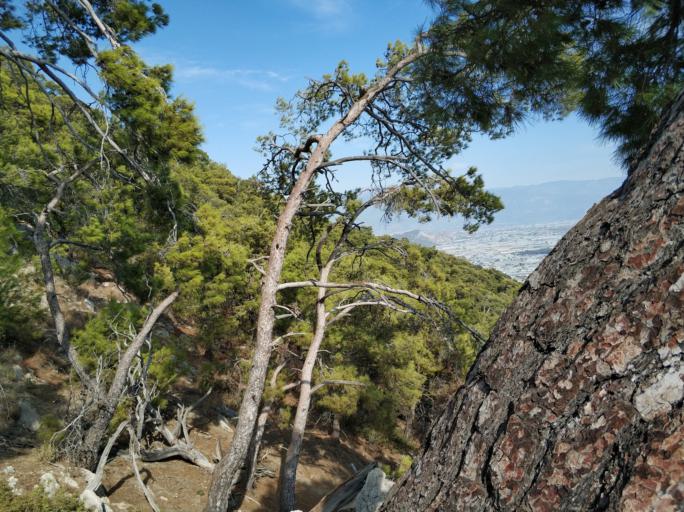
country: TR
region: Mugla
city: Esen
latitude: 36.3346
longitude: 29.2185
